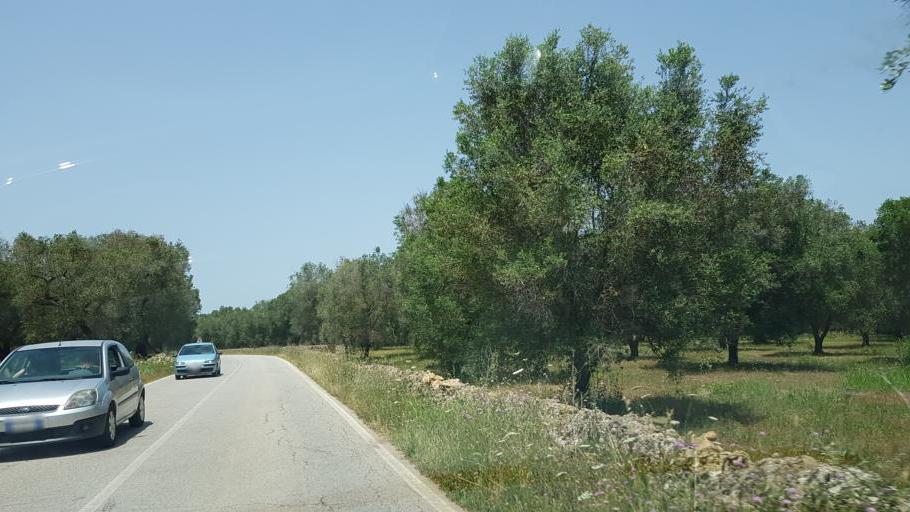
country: IT
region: Apulia
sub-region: Provincia di Brindisi
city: Mesagne
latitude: 40.5157
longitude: 17.8261
